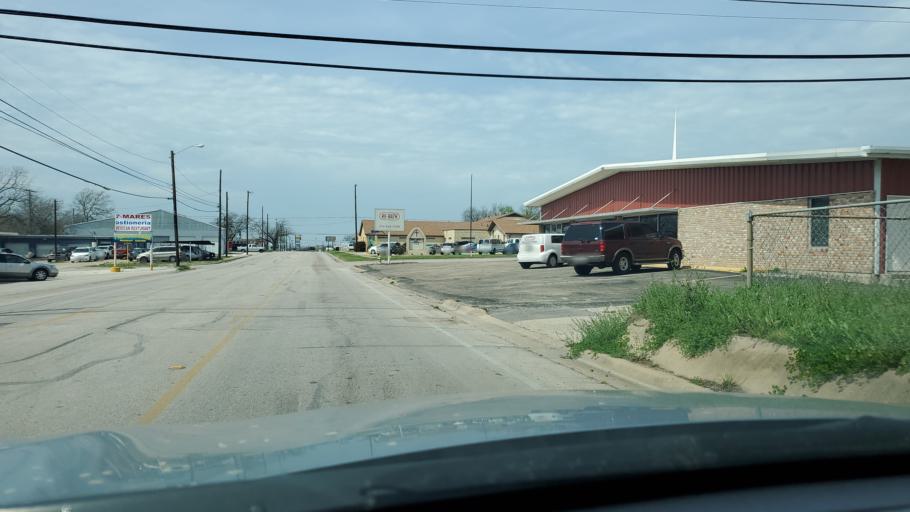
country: US
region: Texas
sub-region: Bell County
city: Temple
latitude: 31.0913
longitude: -97.3714
